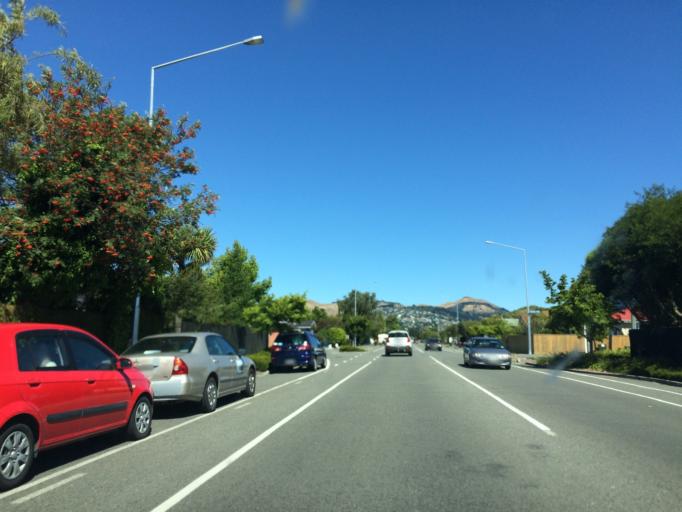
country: NZ
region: Canterbury
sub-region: Christchurch City
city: Christchurch
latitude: -43.5539
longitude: 172.6051
